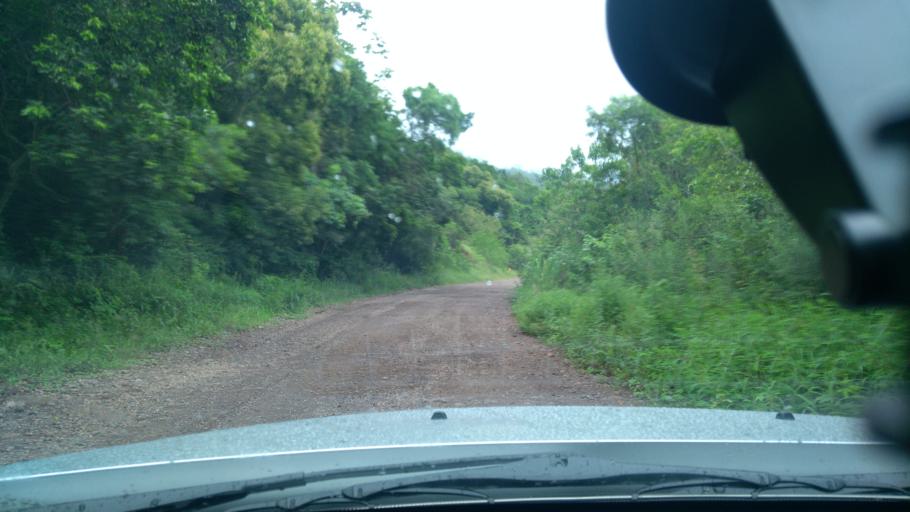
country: BR
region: Rio Grande do Sul
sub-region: Torres
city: Torres
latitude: -29.1969
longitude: -49.9726
